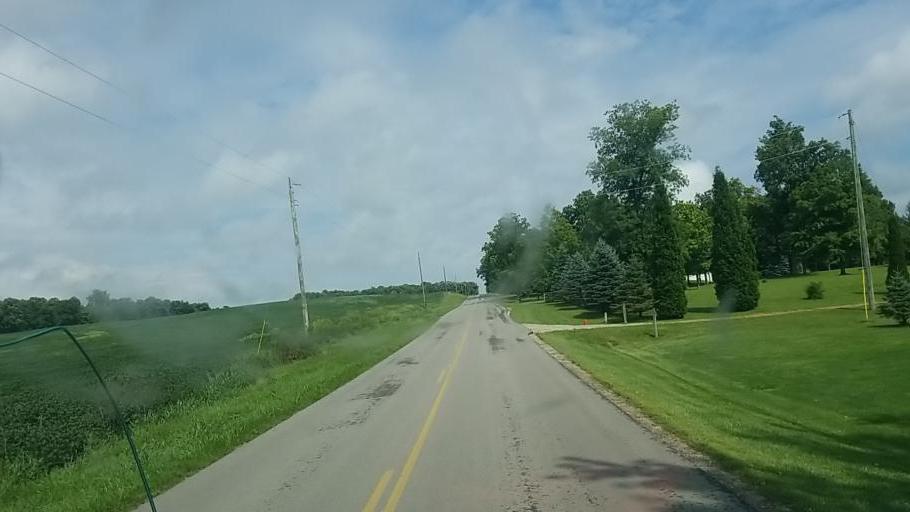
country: US
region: Ohio
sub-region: Logan County
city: West Liberty
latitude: 40.2376
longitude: -83.6592
